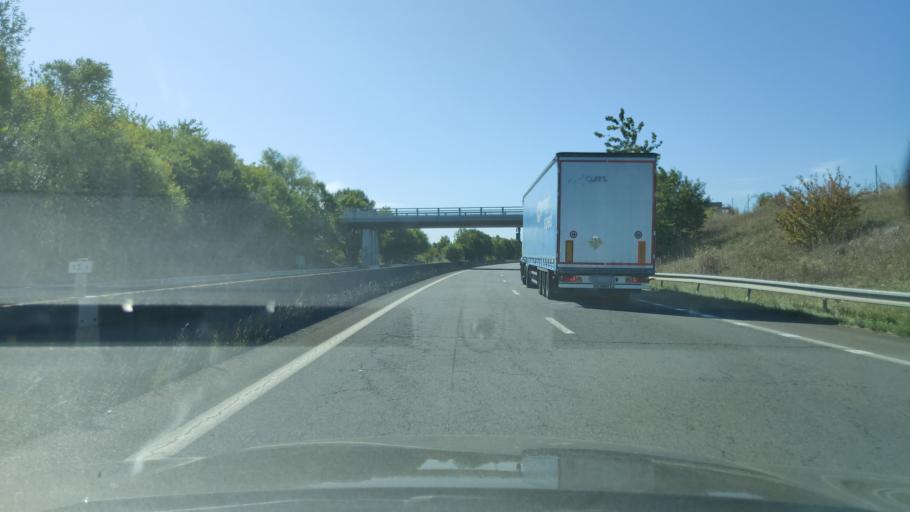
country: FR
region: Lorraine
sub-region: Departement de la Moselle
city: Augny
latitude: 49.0396
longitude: 6.1328
